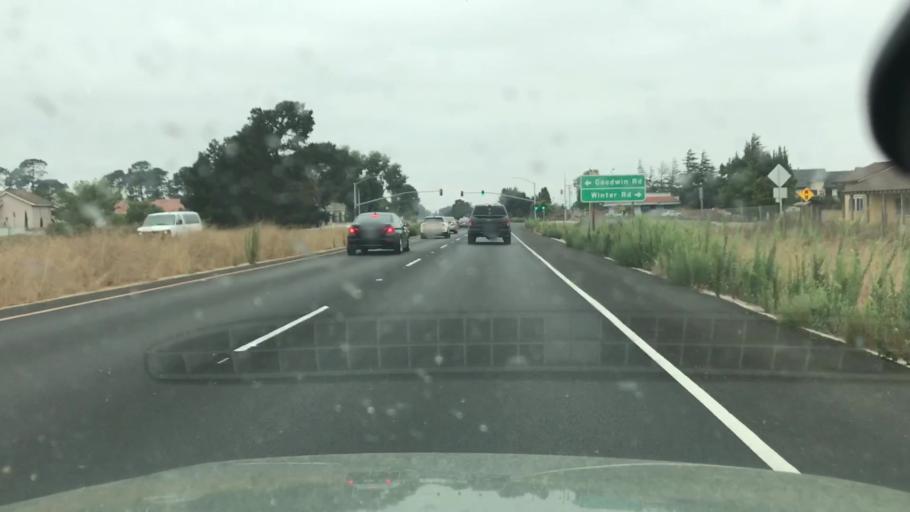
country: US
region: California
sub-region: Santa Barbara County
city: Orcutt
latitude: 34.8974
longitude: -120.4364
